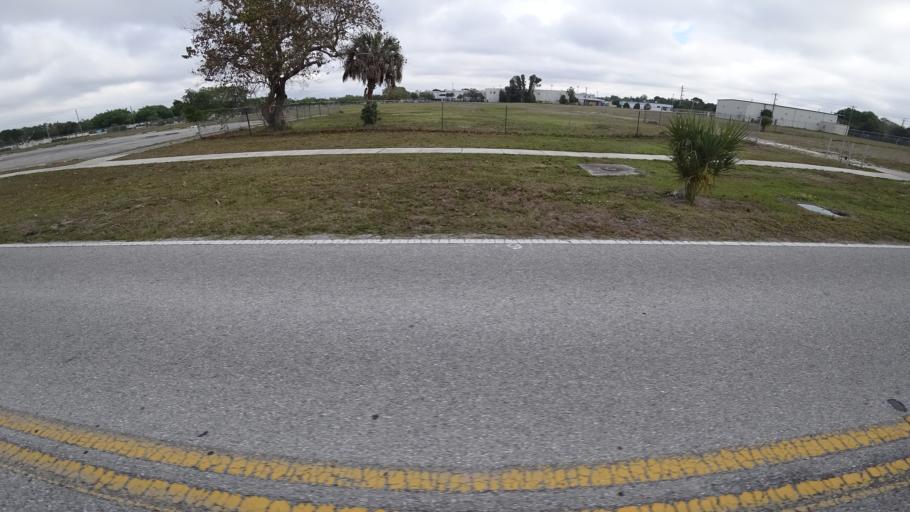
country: US
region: Florida
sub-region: Manatee County
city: Bayshore Gardens
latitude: 27.4404
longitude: -82.5940
